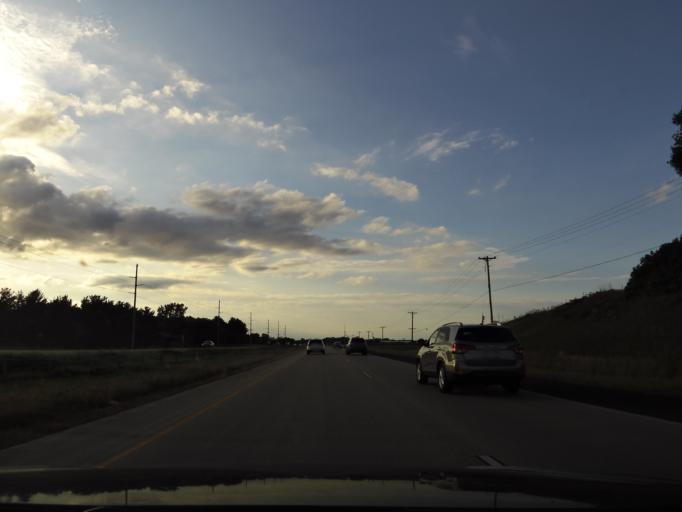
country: US
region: Minnesota
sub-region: Dakota County
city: Hastings
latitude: 44.7866
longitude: -92.8791
